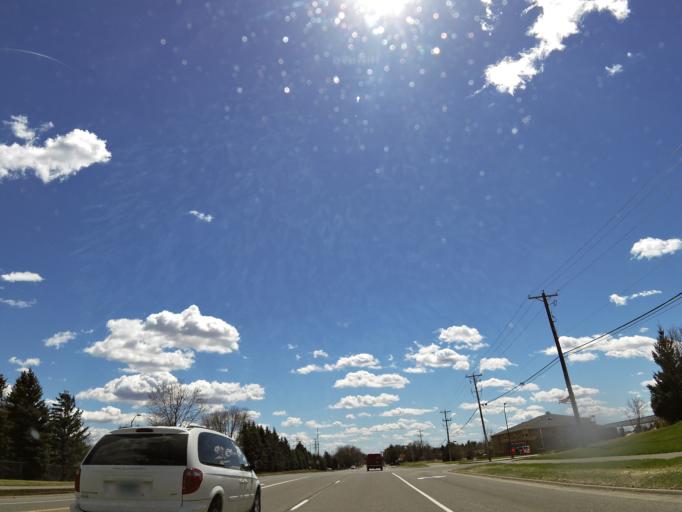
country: US
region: Minnesota
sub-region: Washington County
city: Cottage Grove
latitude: 44.8508
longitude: -92.9492
